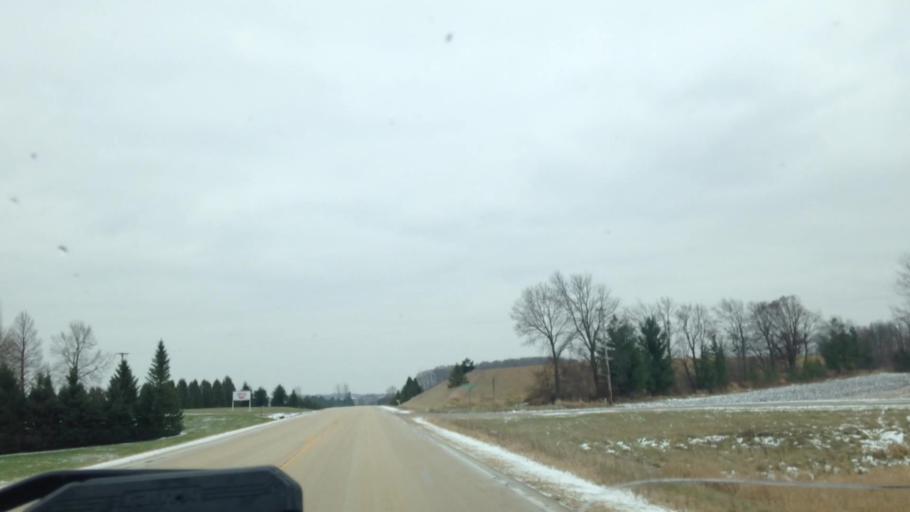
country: US
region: Wisconsin
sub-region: Dodge County
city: Mayville
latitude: 43.4867
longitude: -88.5141
